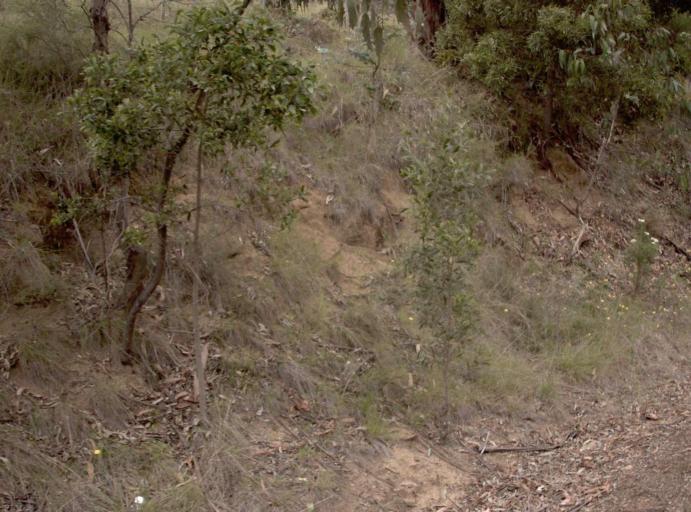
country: AU
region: Victoria
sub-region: East Gippsland
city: Bairnsdale
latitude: -37.5889
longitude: 147.1845
